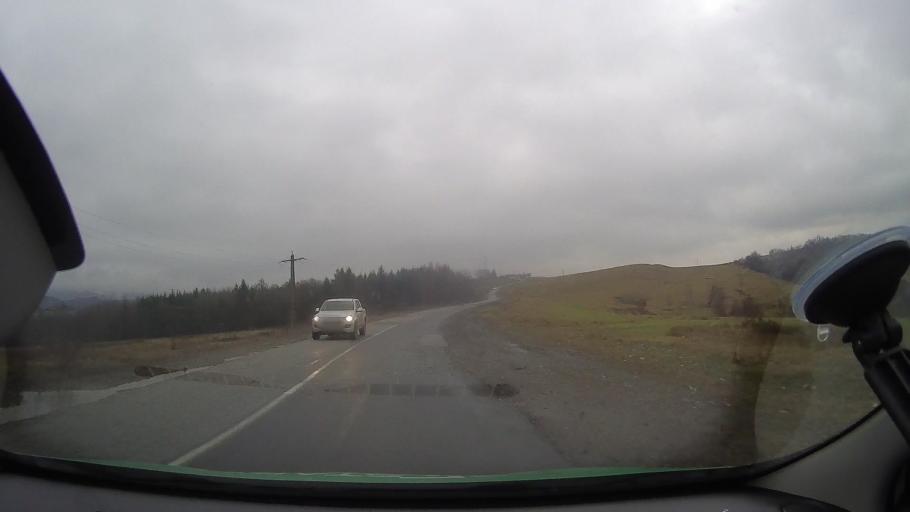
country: RO
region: Arad
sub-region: Comuna Halmagiu
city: Halmagiu
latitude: 46.2862
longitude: 22.5644
